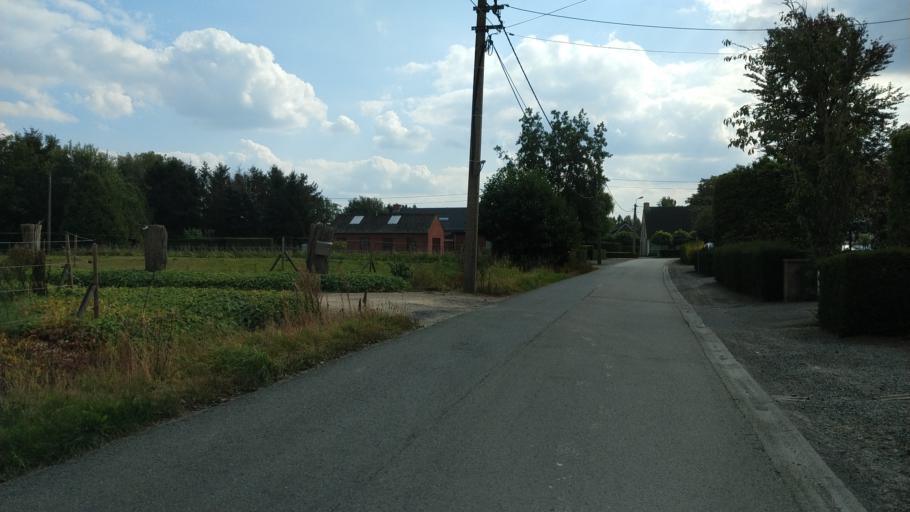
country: BE
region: Flanders
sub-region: Provincie Oost-Vlaanderen
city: Evergem
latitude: 51.1117
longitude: 3.6685
